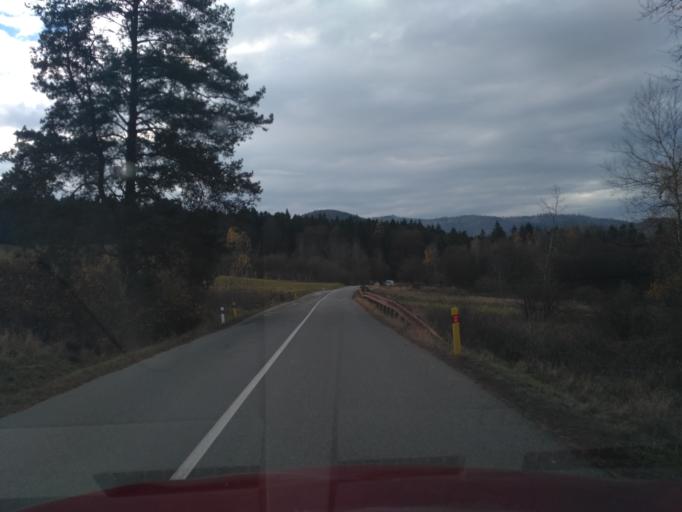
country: SK
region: Kosicky
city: Medzev
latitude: 48.7901
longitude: 20.7744
